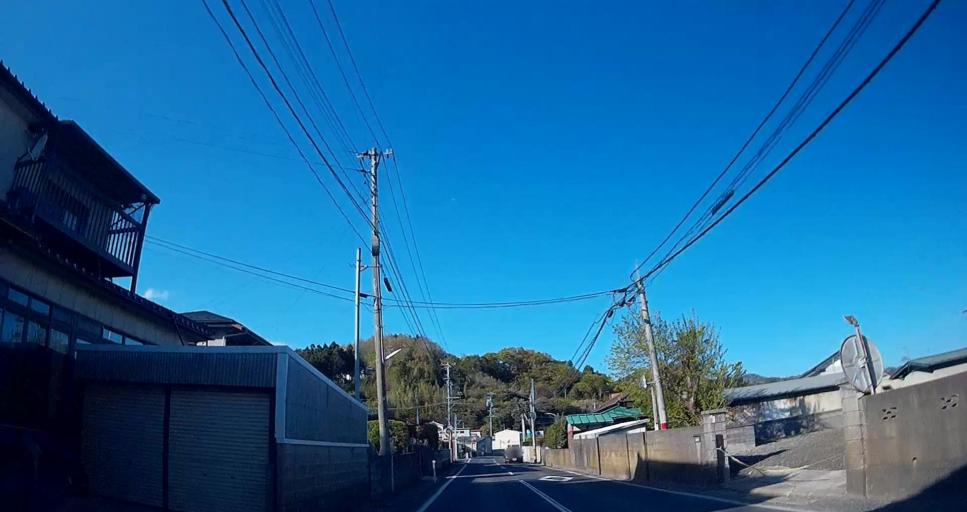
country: JP
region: Miyagi
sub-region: Oshika Gun
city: Onagawa Cho
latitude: 38.4327
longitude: 141.3822
